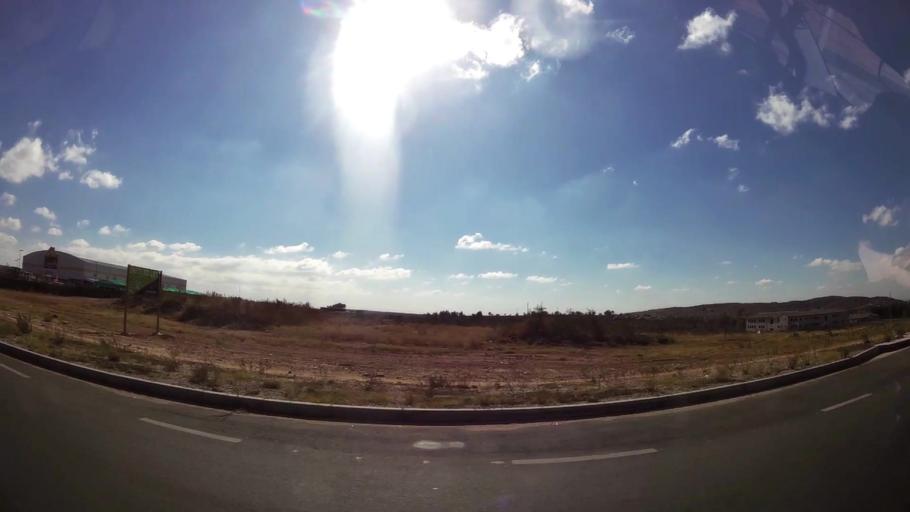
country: ZA
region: Gauteng
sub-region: West Rand District Municipality
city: Krugersdorp
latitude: -26.0843
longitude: 27.8064
